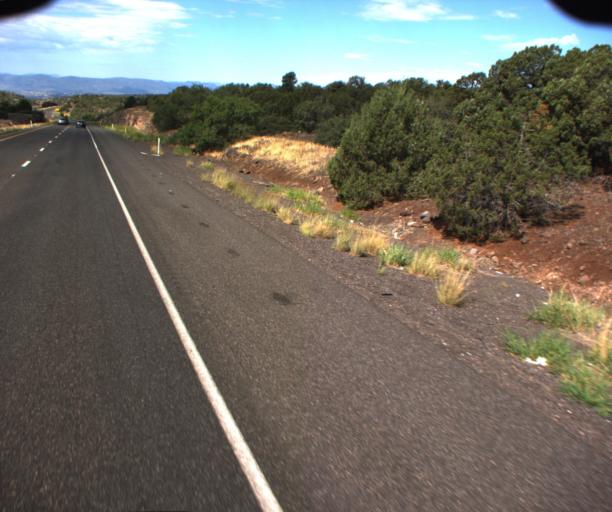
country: US
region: Arizona
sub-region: Yavapai County
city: Big Park
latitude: 34.7309
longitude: -111.7055
